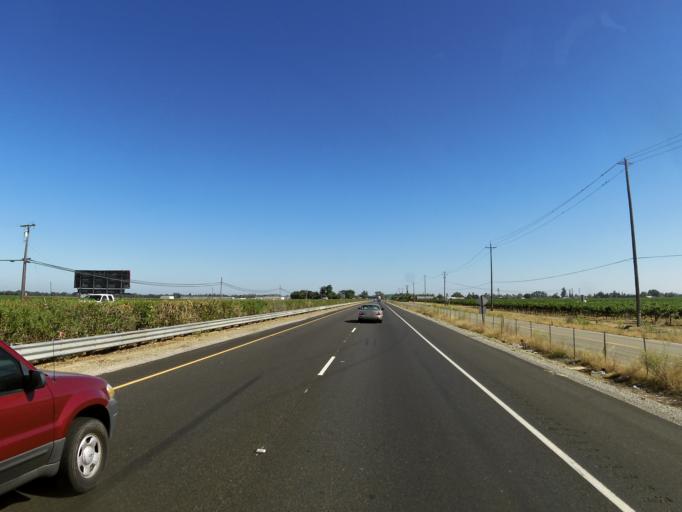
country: US
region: California
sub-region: San Joaquin County
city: Collierville
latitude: 38.1930
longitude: -121.2627
